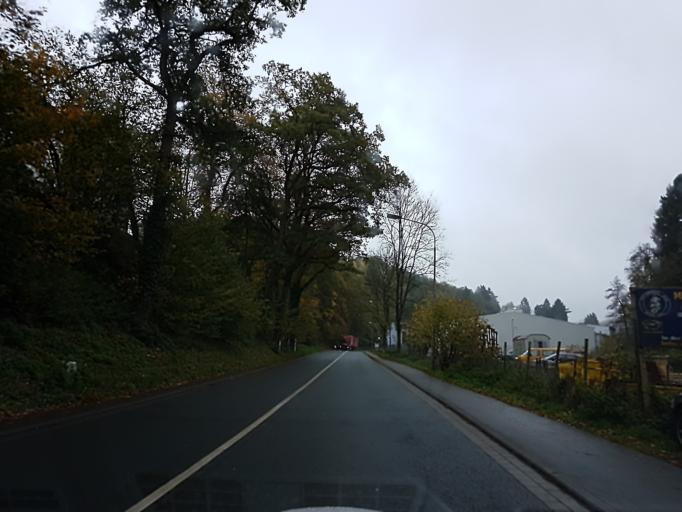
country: DE
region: North Rhine-Westphalia
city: Kierspe
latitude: 51.1349
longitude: 7.6176
